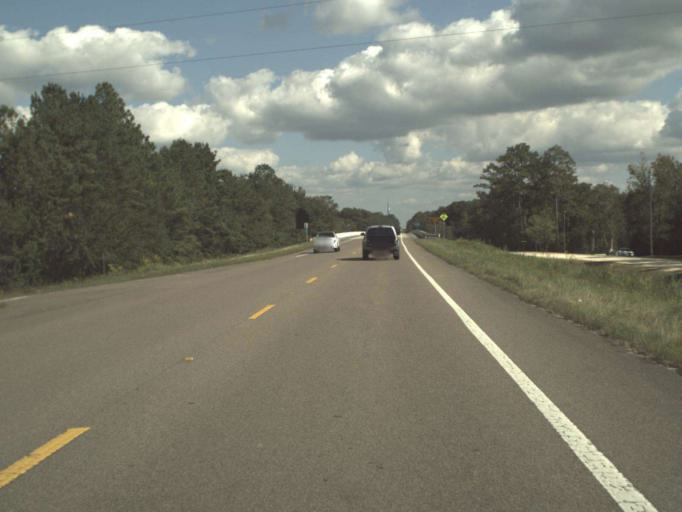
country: US
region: Florida
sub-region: Bay County
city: Laguna Beach
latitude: 30.4522
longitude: -85.9018
